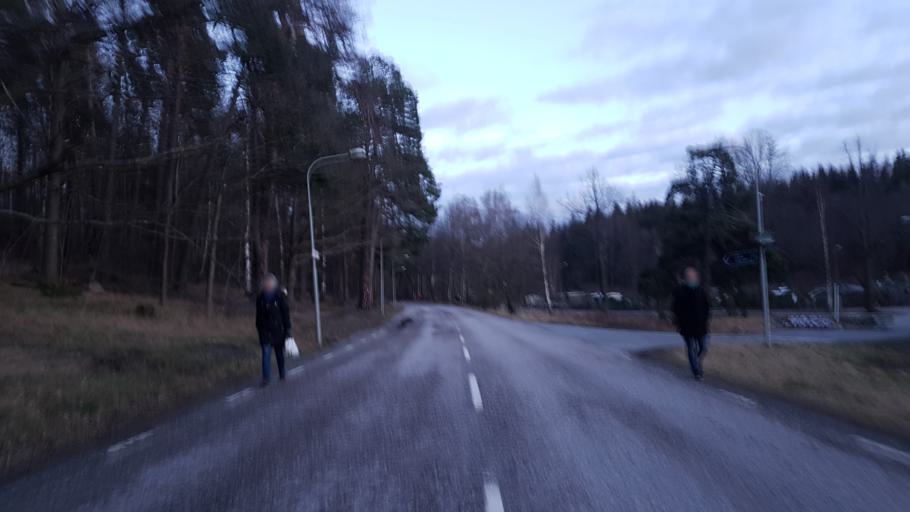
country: SE
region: Stockholm
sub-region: Stockholms Kommun
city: Stockholm
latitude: 59.3573
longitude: 18.0628
